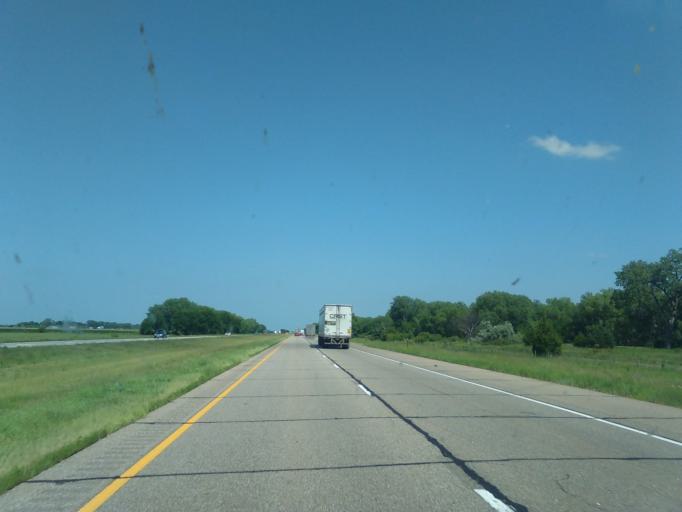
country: US
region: Nebraska
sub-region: Buffalo County
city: Kearney
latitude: 40.6723
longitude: -99.2031
